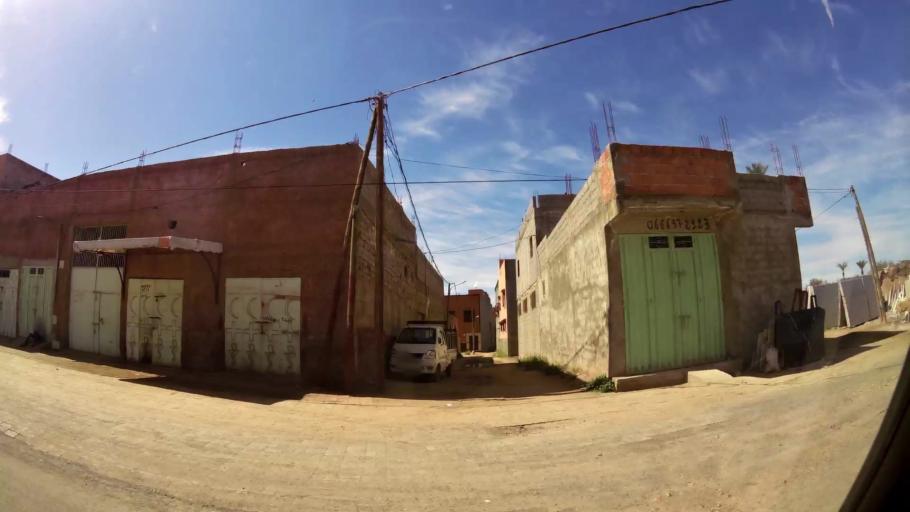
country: MA
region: Marrakech-Tensift-Al Haouz
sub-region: Marrakech
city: Marrakesh
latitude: 31.6304
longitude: -7.9576
